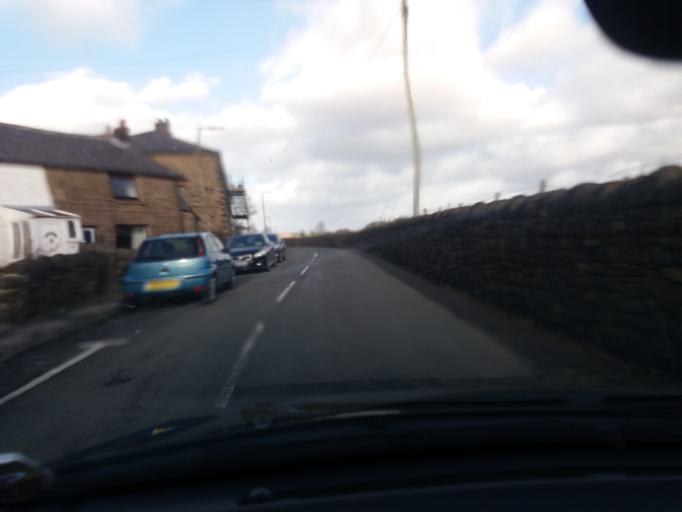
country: GB
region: England
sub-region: Lancashire
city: Adlington
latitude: 53.6236
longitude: -2.5903
